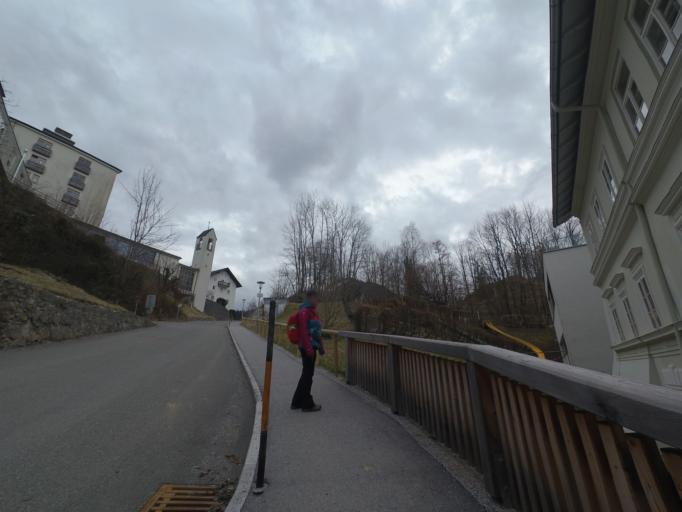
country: AT
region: Salzburg
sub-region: Politischer Bezirk Hallein
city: Hallein
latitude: 47.6650
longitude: 13.0899
